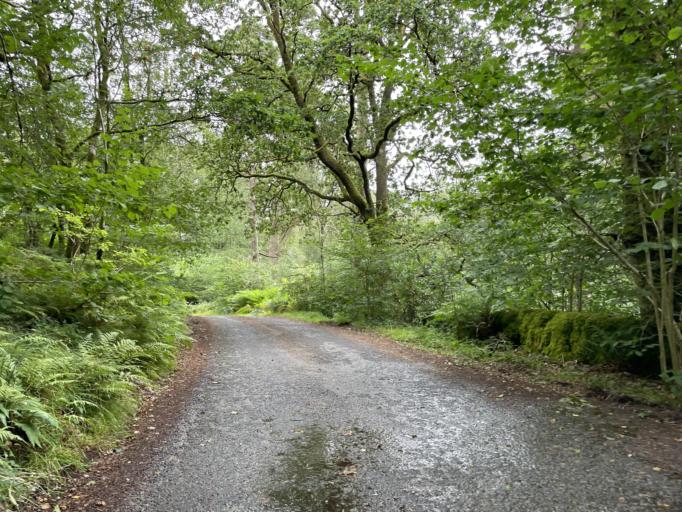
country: GB
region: Scotland
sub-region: Dumfries and Galloway
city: Newton Stewart
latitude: 55.0906
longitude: -4.4980
